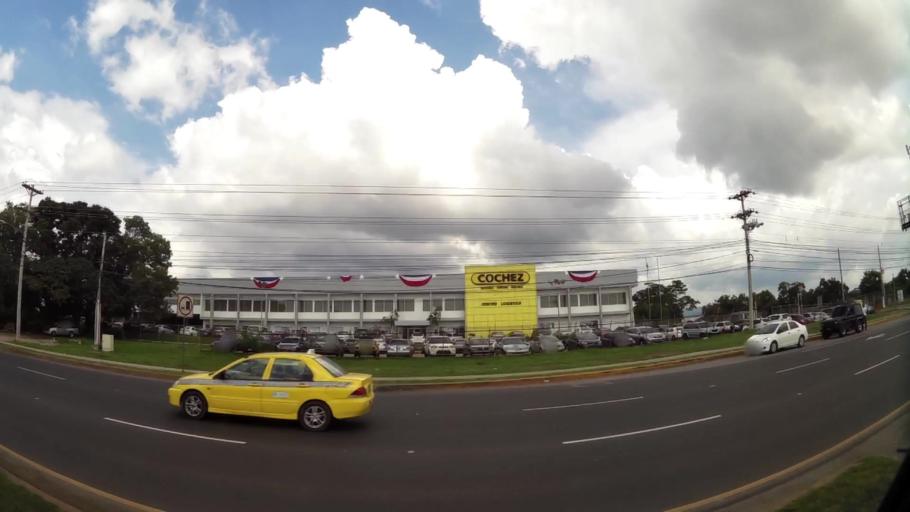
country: PA
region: Panama
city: Tocumen
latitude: 9.0684
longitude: -79.4082
